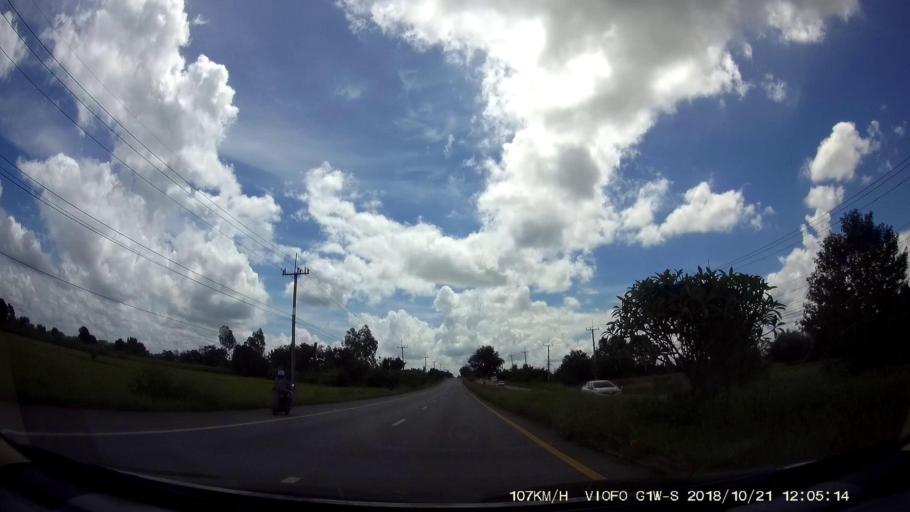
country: TH
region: Chaiyaphum
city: Chatturat
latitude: 15.4819
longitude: 101.8231
